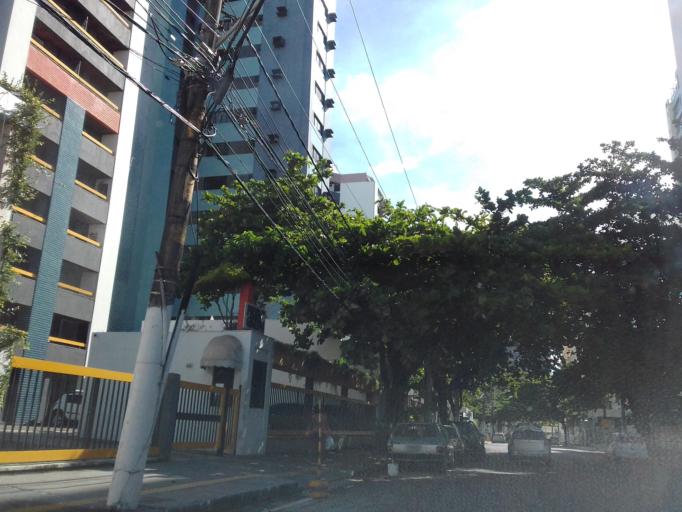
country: BR
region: Bahia
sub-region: Salvador
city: Salvador
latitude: -13.0021
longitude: -38.4571
